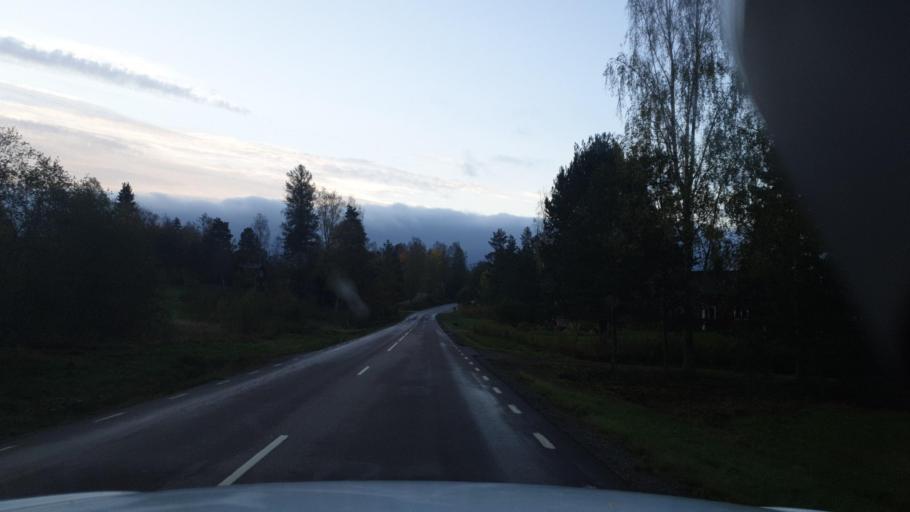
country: SE
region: Vaermland
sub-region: Arvika Kommun
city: Arvika
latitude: 59.8013
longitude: 12.6046
